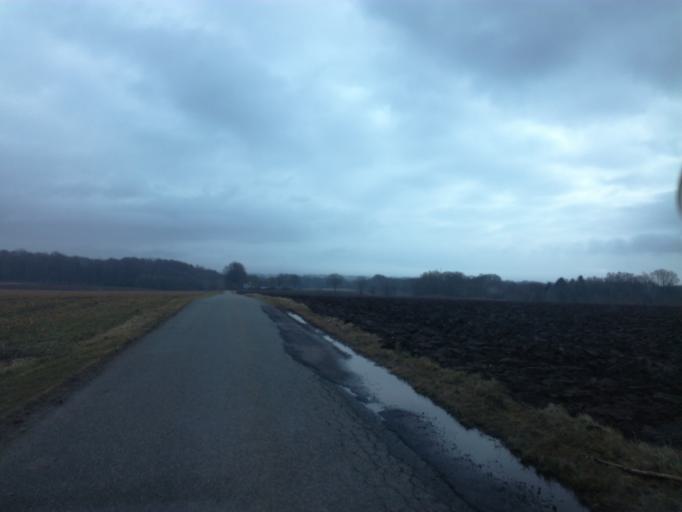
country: DK
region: South Denmark
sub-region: Vejle Kommune
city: Brejning
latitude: 55.6186
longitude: 9.6968
